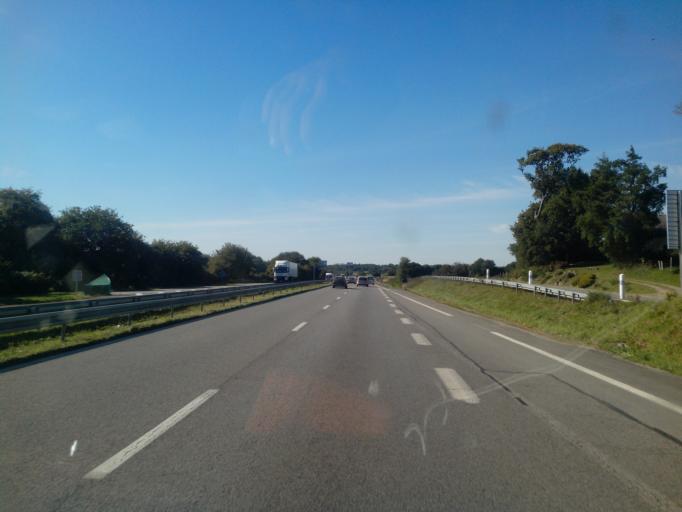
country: FR
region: Brittany
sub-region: Departement du Morbihan
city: Ambon
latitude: 47.5898
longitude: -2.5518
